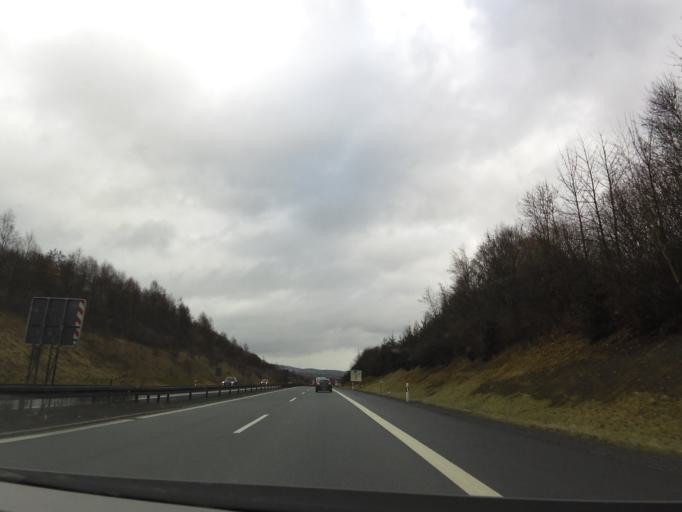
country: DE
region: Bavaria
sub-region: Upper Franconia
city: Selb
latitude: 50.1879
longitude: 12.1099
